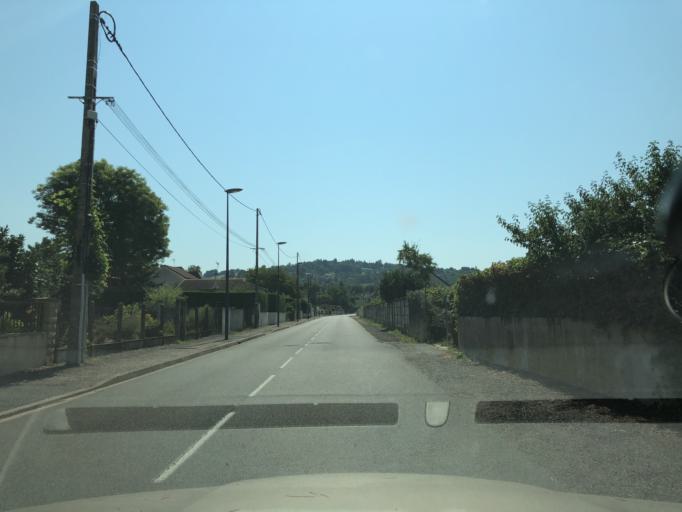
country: FR
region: Auvergne
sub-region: Departement de l'Allier
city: Cusset
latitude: 46.1333
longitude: 3.4627
